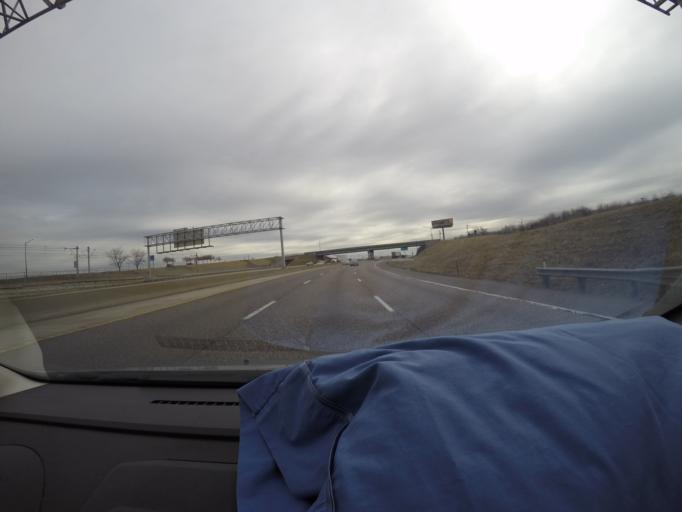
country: US
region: Missouri
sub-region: Saint Louis County
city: Woodson Terrace
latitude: 38.7332
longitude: -90.3460
